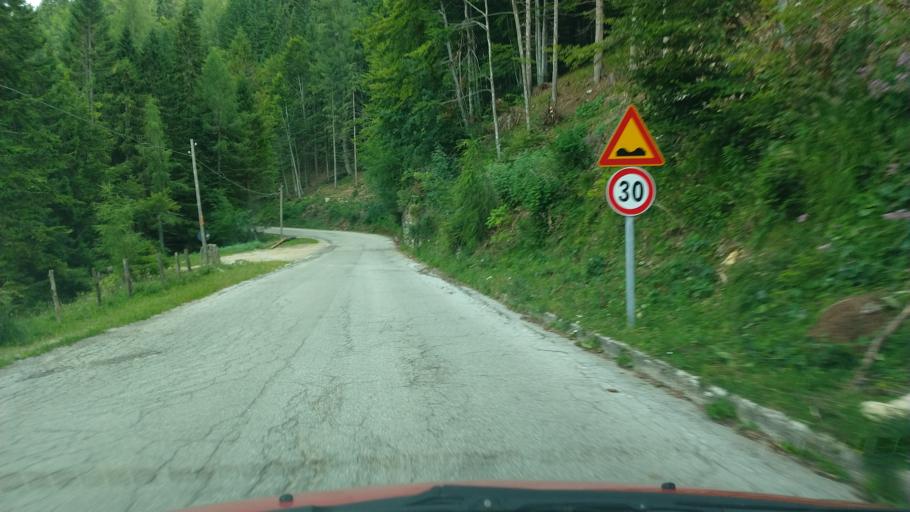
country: IT
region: Veneto
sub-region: Provincia di Vicenza
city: Pedemonte
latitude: 45.8827
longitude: 11.2937
